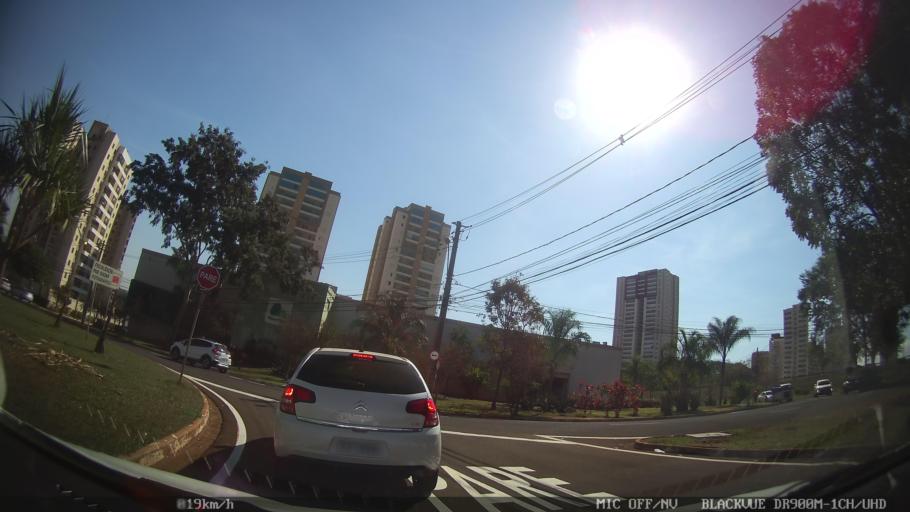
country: BR
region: Sao Paulo
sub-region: Ribeirao Preto
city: Ribeirao Preto
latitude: -21.2208
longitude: -47.8283
